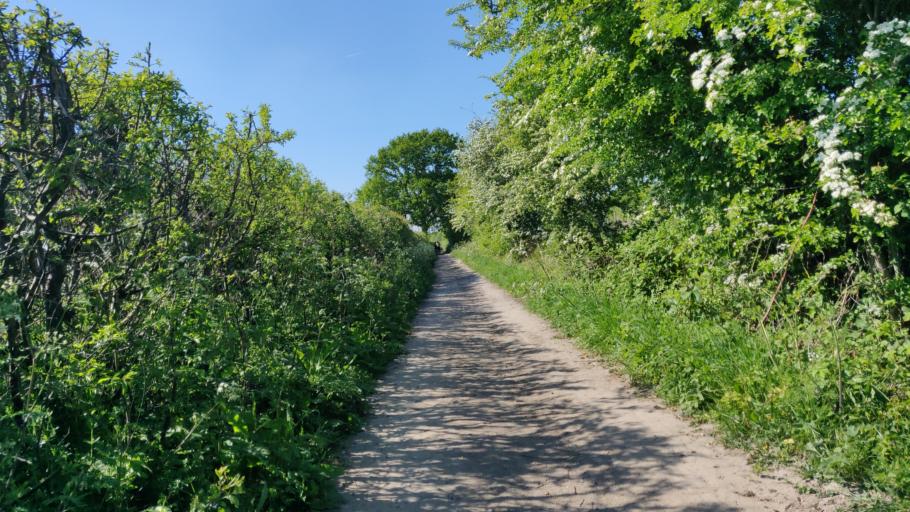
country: GB
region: England
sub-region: West Sussex
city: Southwater
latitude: 51.0562
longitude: -0.3780
